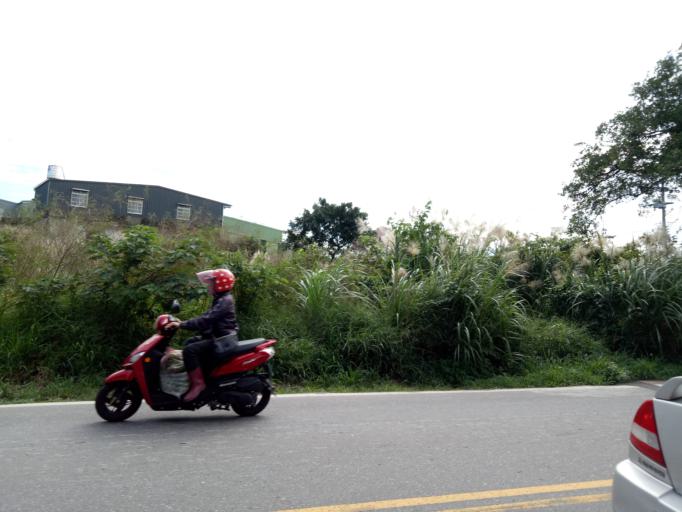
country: TW
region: Taiwan
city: Daxi
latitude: 24.9280
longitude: 121.3144
